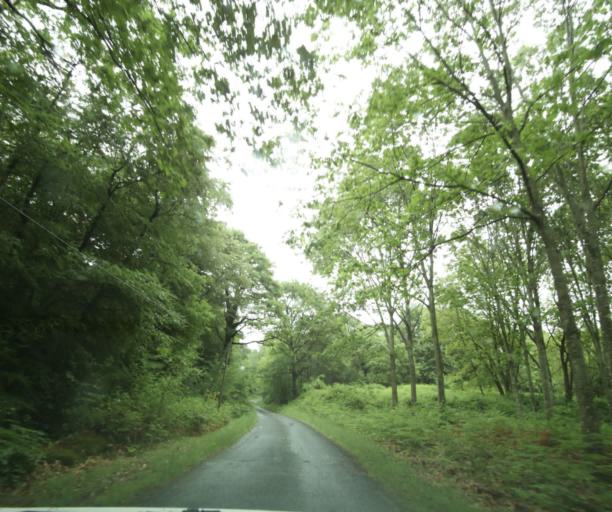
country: FR
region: Bourgogne
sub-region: Departement de Saone-et-Loire
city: Palinges
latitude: 46.5345
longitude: 4.2629
